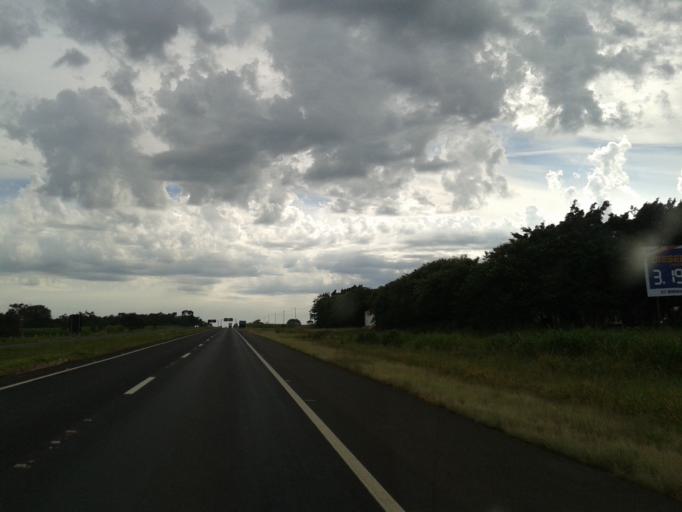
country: BR
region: Minas Gerais
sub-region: Monte Alegre De Minas
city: Monte Alegre de Minas
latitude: -18.8911
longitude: -48.6358
